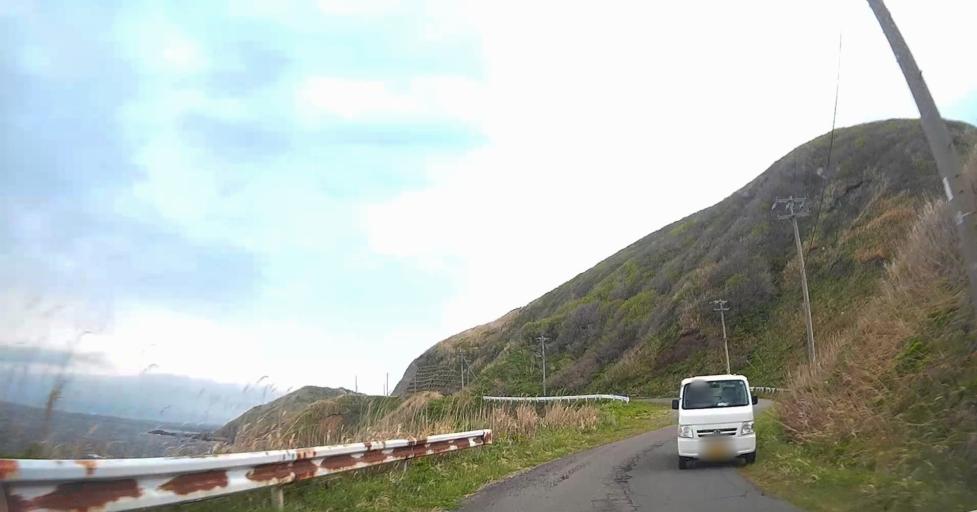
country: JP
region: Aomori
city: Shimokizukuri
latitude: 41.2466
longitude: 140.3435
